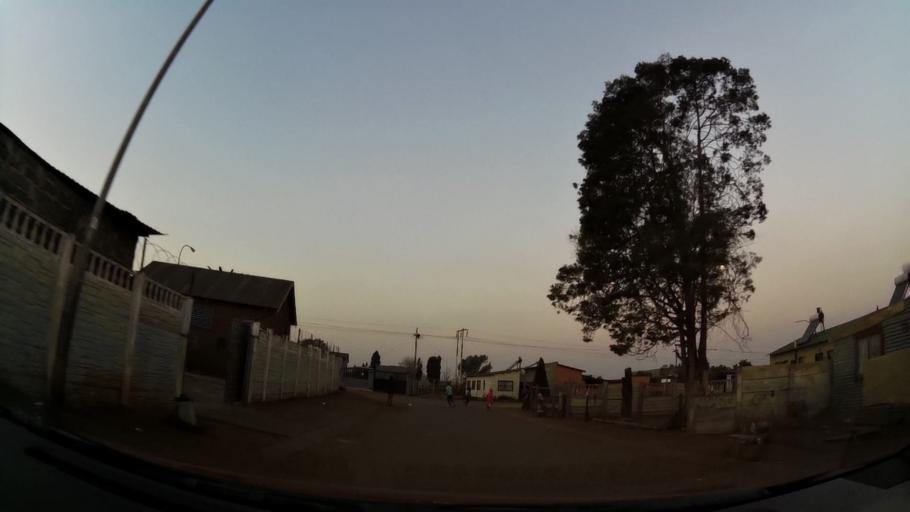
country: ZA
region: Gauteng
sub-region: City of Johannesburg Metropolitan Municipality
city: Soweto
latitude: -26.2944
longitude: 27.8709
